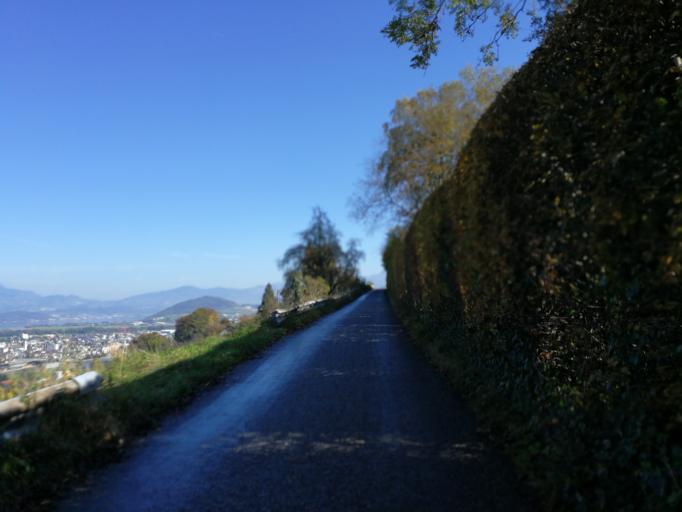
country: CH
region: Schwyz
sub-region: Bezirk March
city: Altendorf
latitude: 47.1834
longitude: 8.8324
